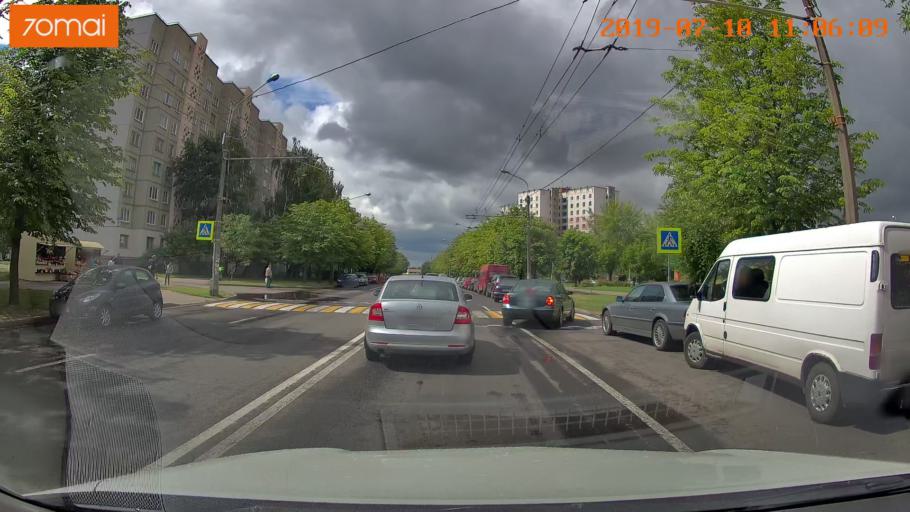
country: BY
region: Minsk
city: Syenitsa
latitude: 53.8508
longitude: 27.5466
